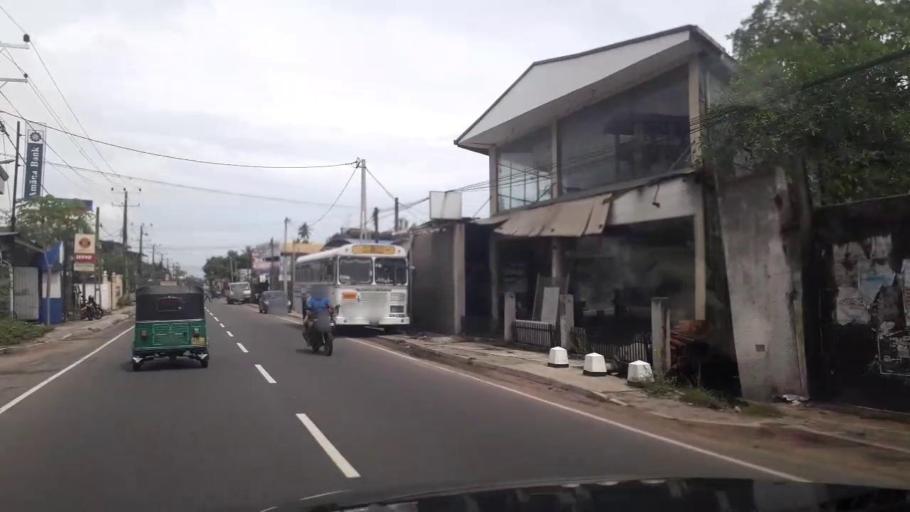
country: LK
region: Western
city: Panadura
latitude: 6.7454
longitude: 79.9018
